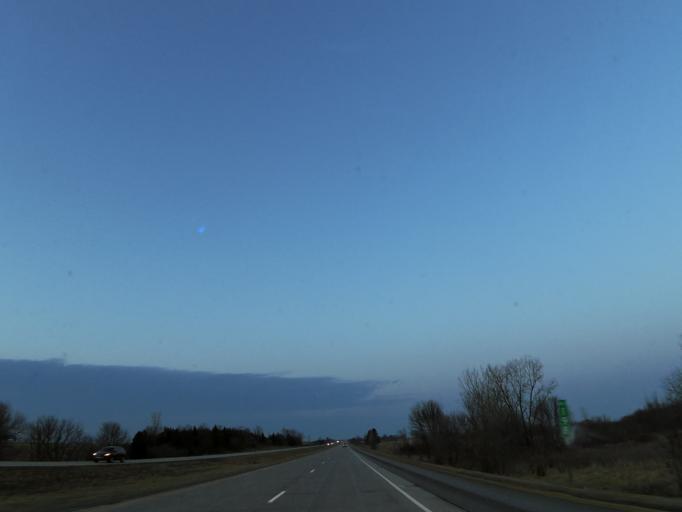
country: US
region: Minnesota
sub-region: Mower County
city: Grand Meadow
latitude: 43.7613
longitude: -92.6414
